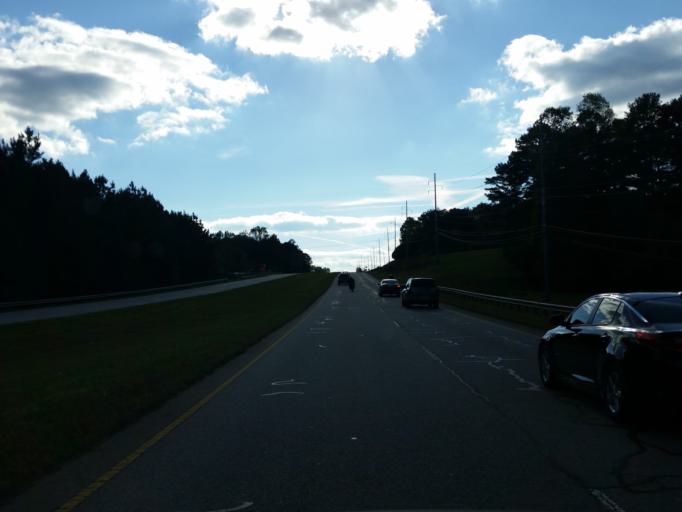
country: US
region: Georgia
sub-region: Paulding County
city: Hiram
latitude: 33.9231
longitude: -84.7556
